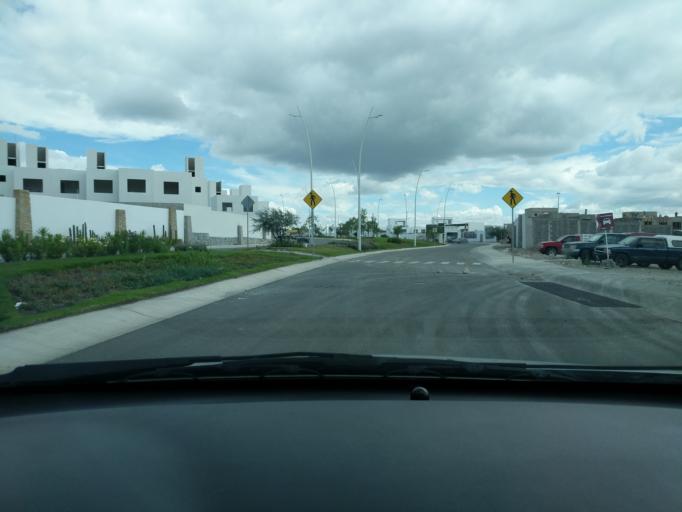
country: MX
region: Queretaro
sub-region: El Marques
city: El Pozo
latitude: 20.6465
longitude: -100.3151
